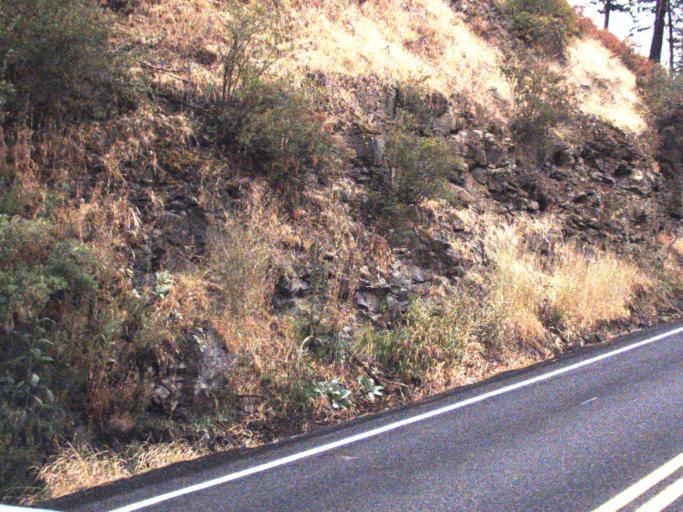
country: US
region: Washington
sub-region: Spokane County
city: Medical Lake
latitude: 47.7449
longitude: -117.8864
